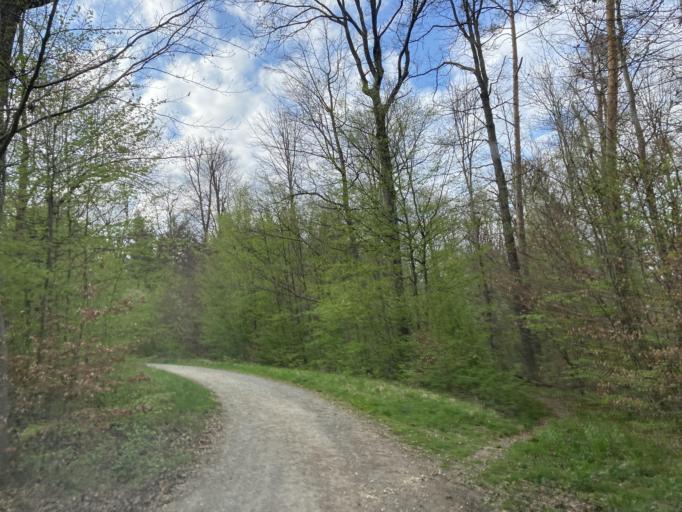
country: DE
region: Baden-Wuerttemberg
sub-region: Tuebingen Region
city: Wannweil
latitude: 48.5156
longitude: 9.1392
